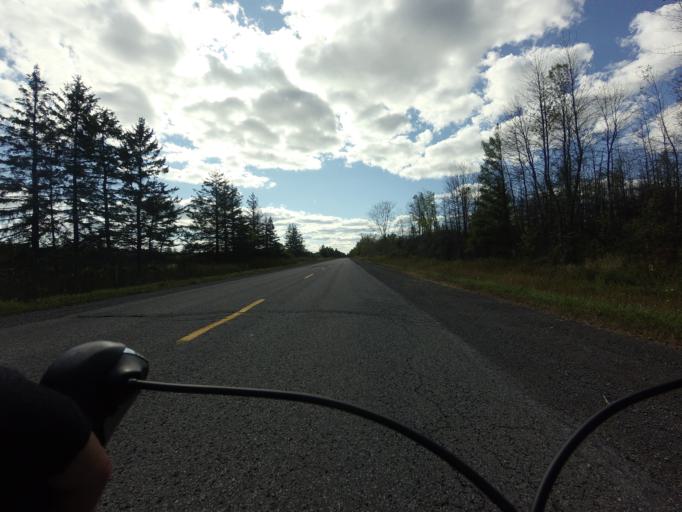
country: CA
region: Ontario
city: Bells Corners
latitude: 45.1043
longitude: -75.6279
